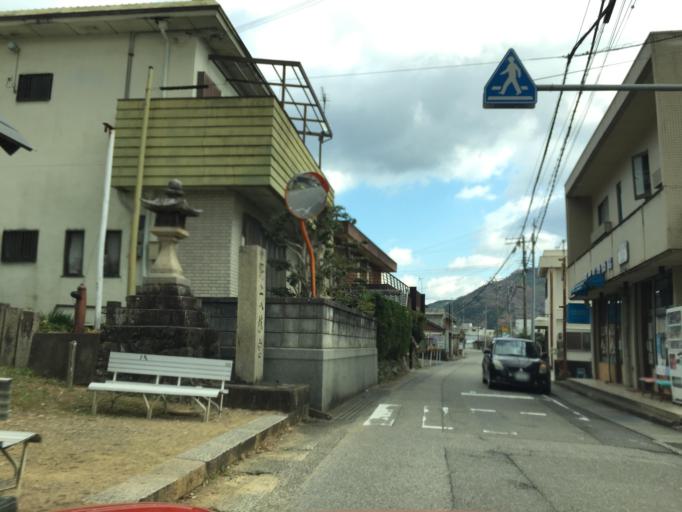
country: JP
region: Wakayama
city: Iwade
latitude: 34.1650
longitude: 135.2948
